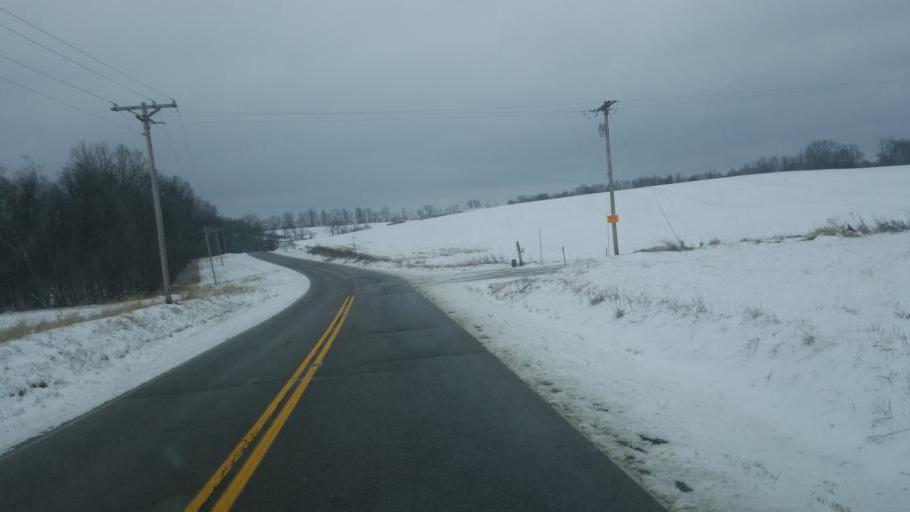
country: US
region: Ohio
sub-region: Knox County
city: Oak Hill
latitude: 40.4324
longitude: -82.1426
